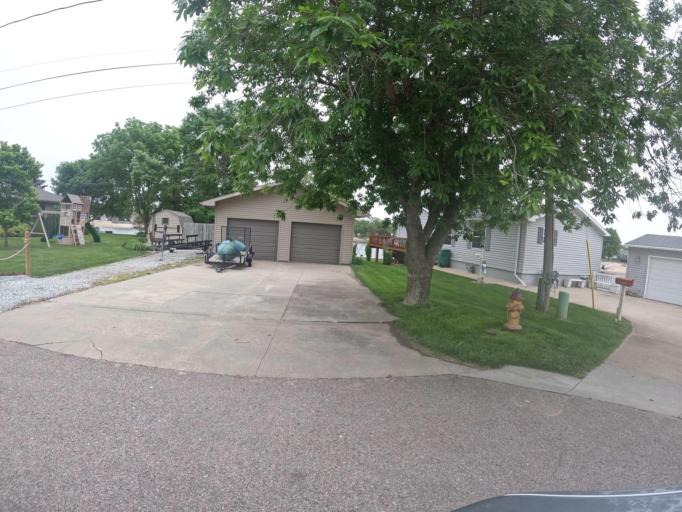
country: US
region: Nebraska
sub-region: Sarpy County
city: Offutt Air Force Base
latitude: 41.0548
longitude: -95.9557
